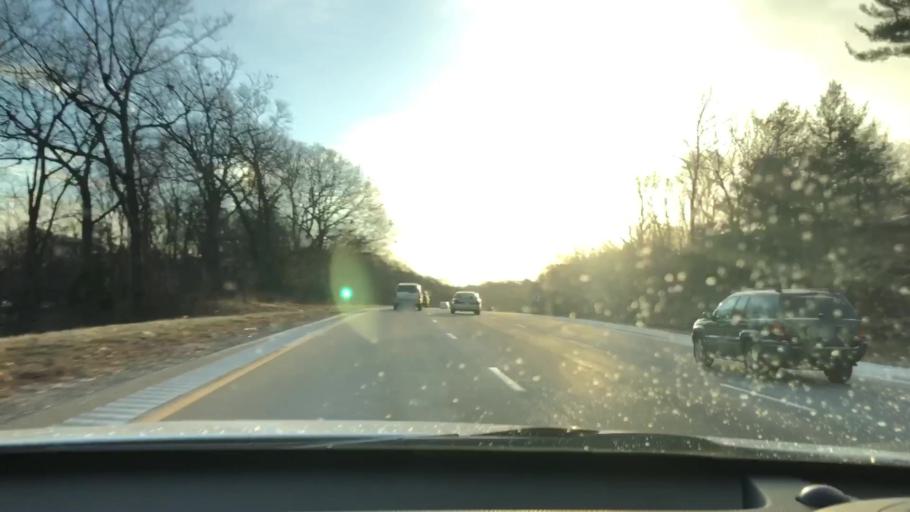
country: US
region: Massachusetts
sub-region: Norfolk County
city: Weymouth
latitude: 42.1927
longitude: -70.9497
